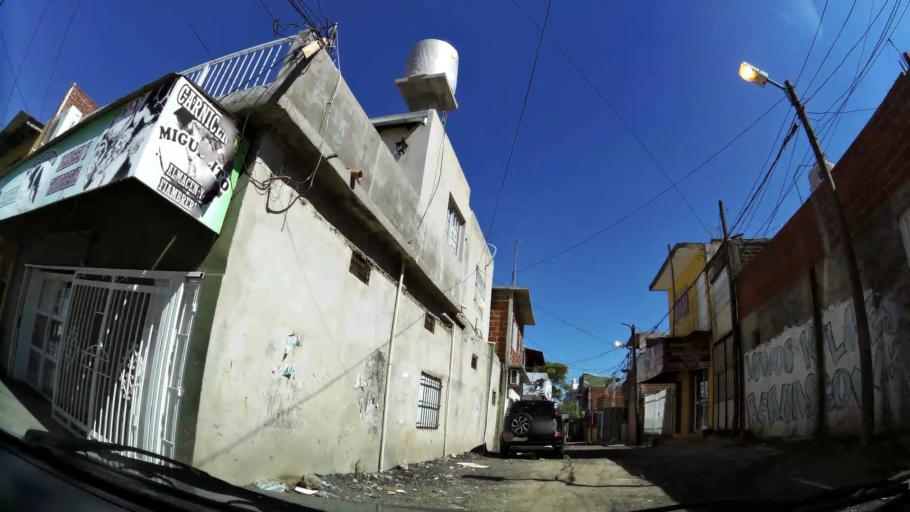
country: AR
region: Buenos Aires
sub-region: Partido de Quilmes
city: Quilmes
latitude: -34.7097
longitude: -58.2971
